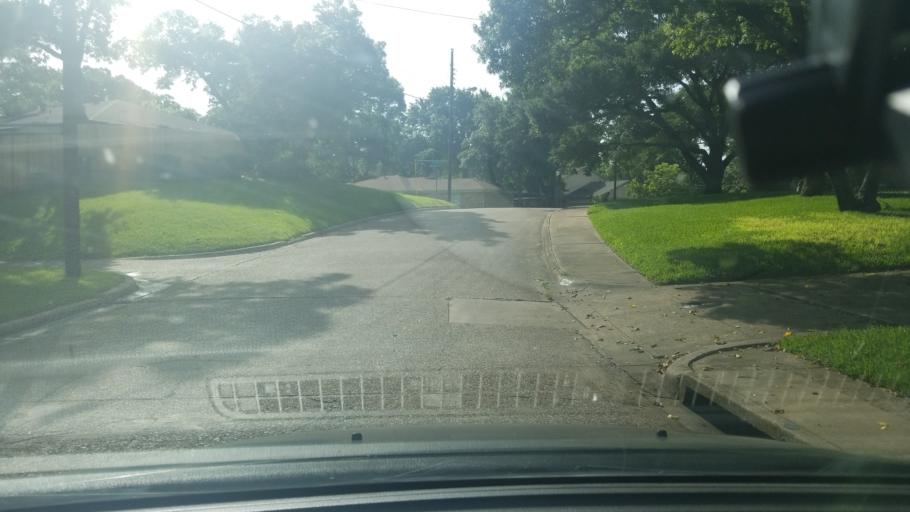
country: US
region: Texas
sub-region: Dallas County
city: Highland Park
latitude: 32.8009
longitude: -96.6989
